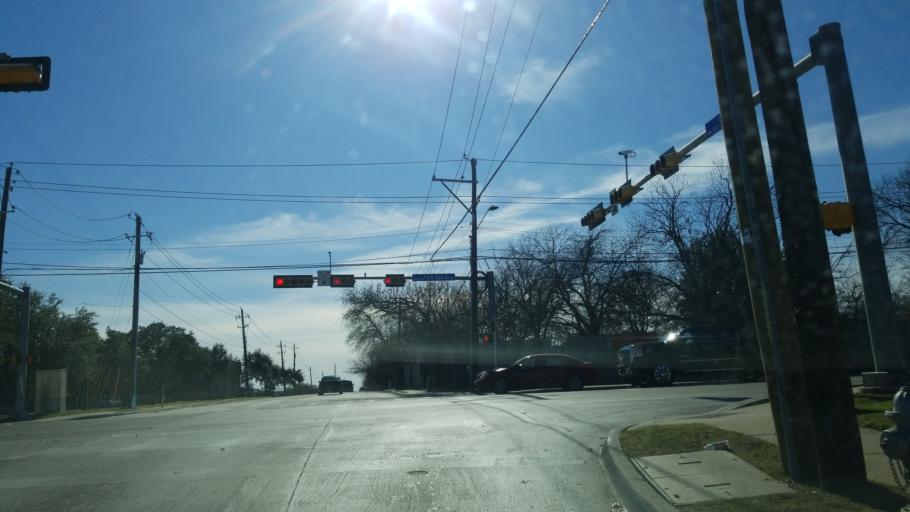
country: US
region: Texas
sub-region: Tarrant County
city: Arlington
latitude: 32.7209
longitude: -97.0572
